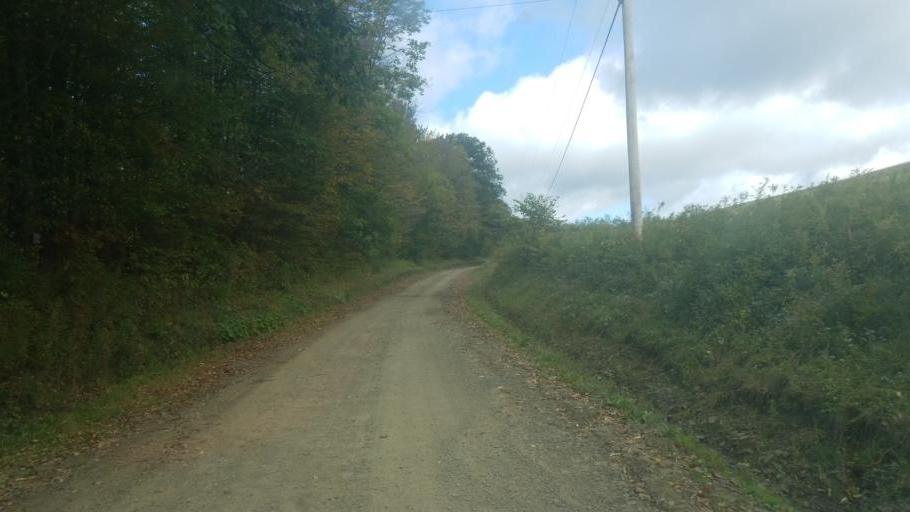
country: US
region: New York
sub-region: Allegany County
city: Cuba
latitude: 42.1338
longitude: -78.3014
